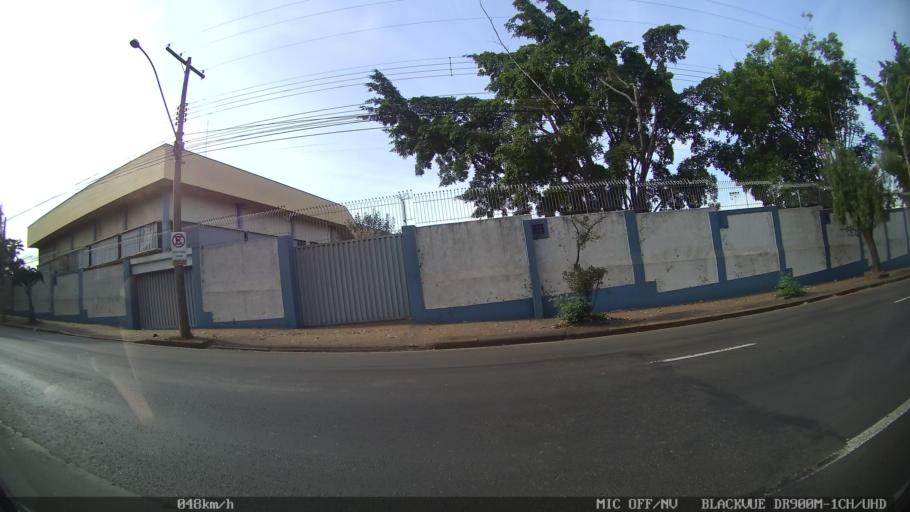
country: BR
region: Sao Paulo
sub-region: Piracicaba
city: Piracicaba
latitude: -22.7000
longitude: -47.6553
